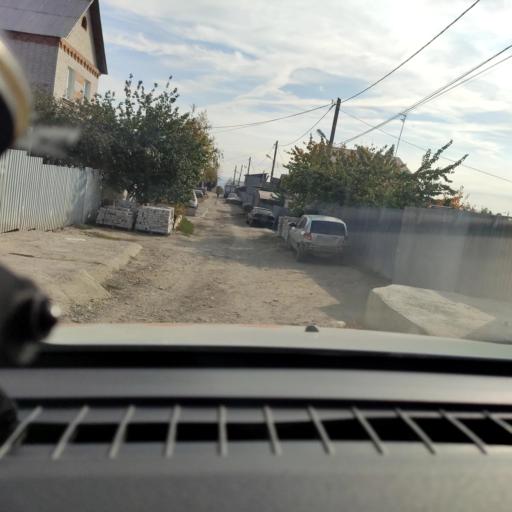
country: RU
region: Samara
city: Samara
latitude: 53.1832
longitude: 50.1792
